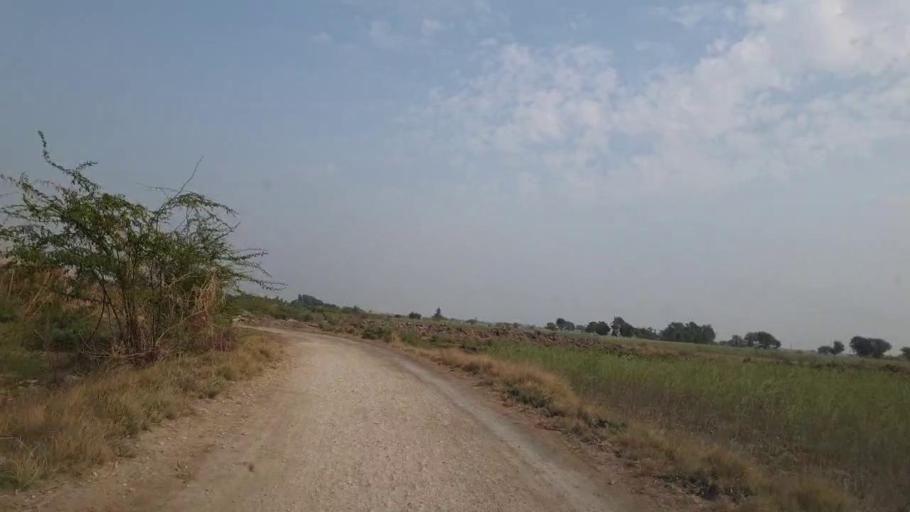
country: PK
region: Sindh
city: Mirpur Khas
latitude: 25.5726
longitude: 69.1541
